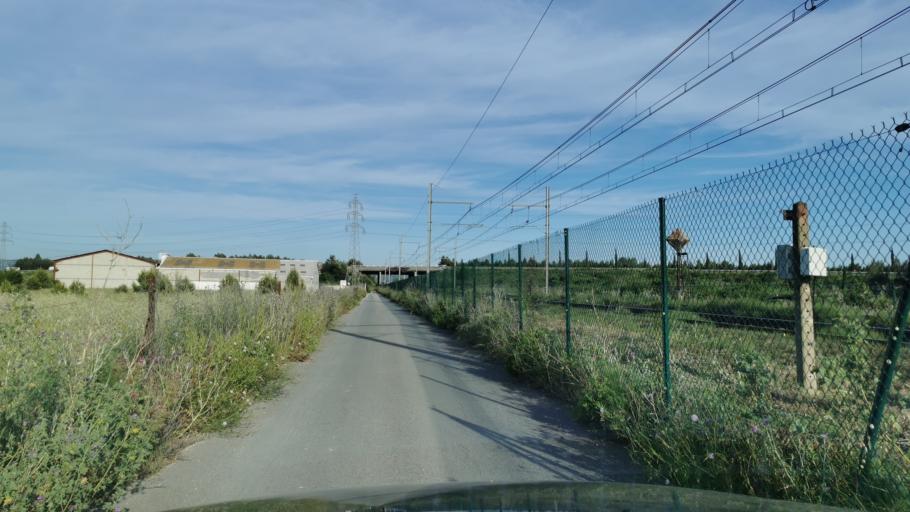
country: FR
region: Languedoc-Roussillon
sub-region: Departement de l'Aude
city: Narbonne
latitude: 43.1671
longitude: 2.9969
